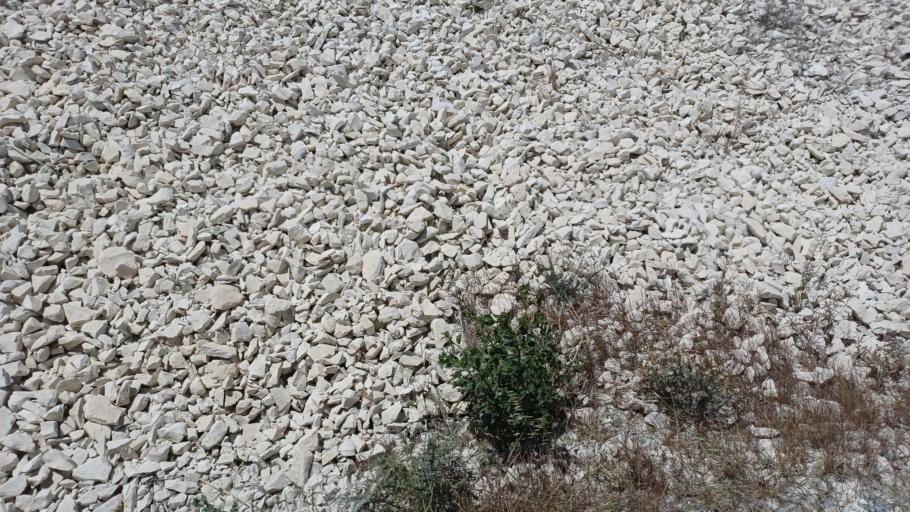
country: CY
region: Larnaka
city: Athienou
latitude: 35.0250
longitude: 33.5287
